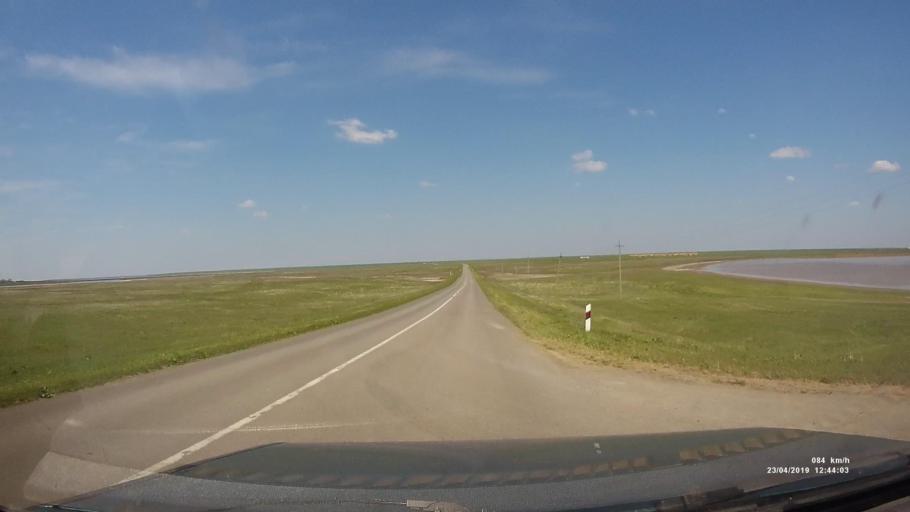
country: RU
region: Kalmykiya
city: Yashalta
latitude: 46.4720
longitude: 42.6493
